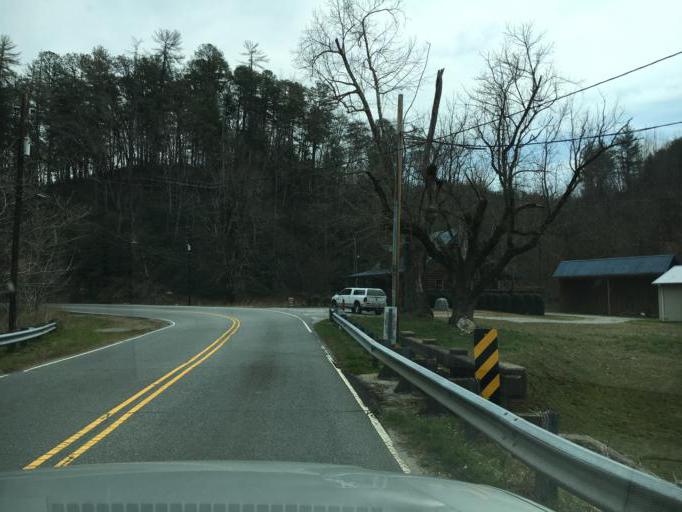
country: US
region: North Carolina
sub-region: Rutherford County
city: Lake Lure
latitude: 35.4220
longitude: -82.1749
